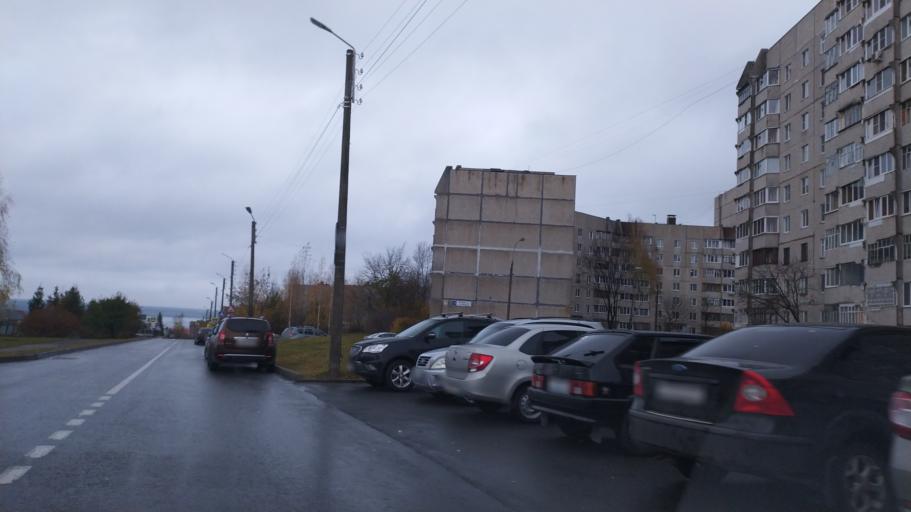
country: RU
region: Chuvashia
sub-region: Cheboksarskiy Rayon
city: Cheboksary
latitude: 56.1442
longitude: 47.1615
